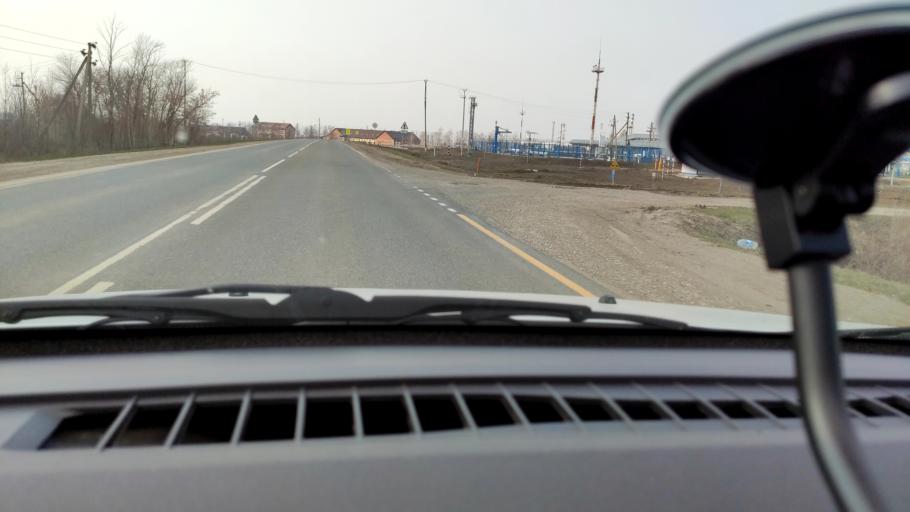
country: RU
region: Samara
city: Dubovyy Umet
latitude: 53.0805
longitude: 50.3482
